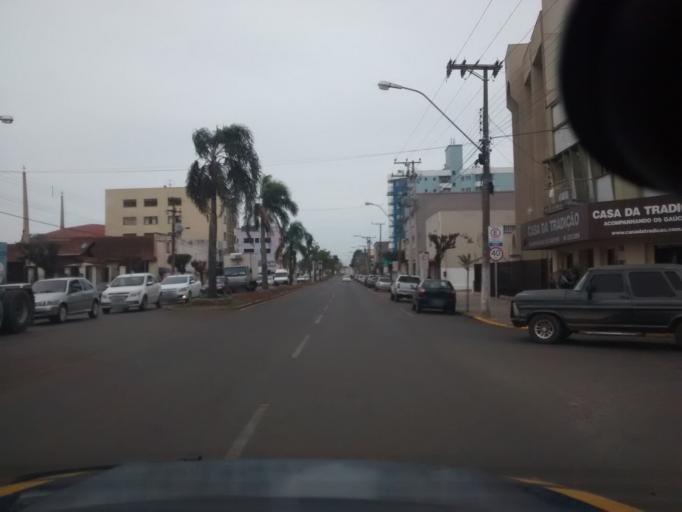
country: BR
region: Rio Grande do Sul
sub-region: Vacaria
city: Vacaria
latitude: -28.5106
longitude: -50.9358
